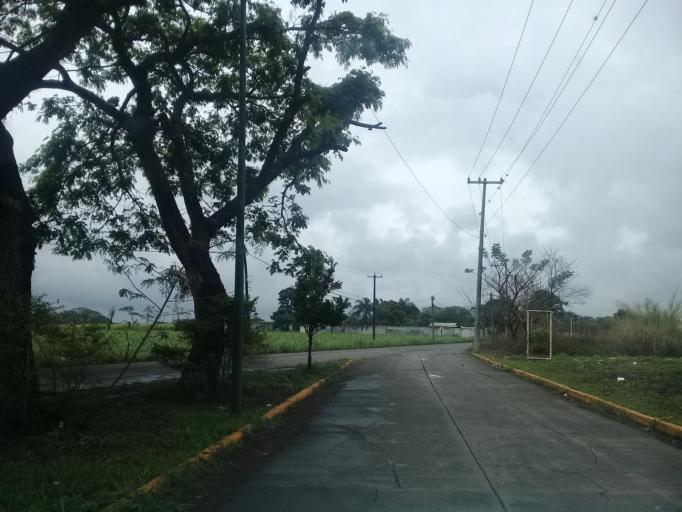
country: MX
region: Veracruz
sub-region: Cordoba
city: San Jose de Tapia
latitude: 18.8387
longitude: -96.9564
